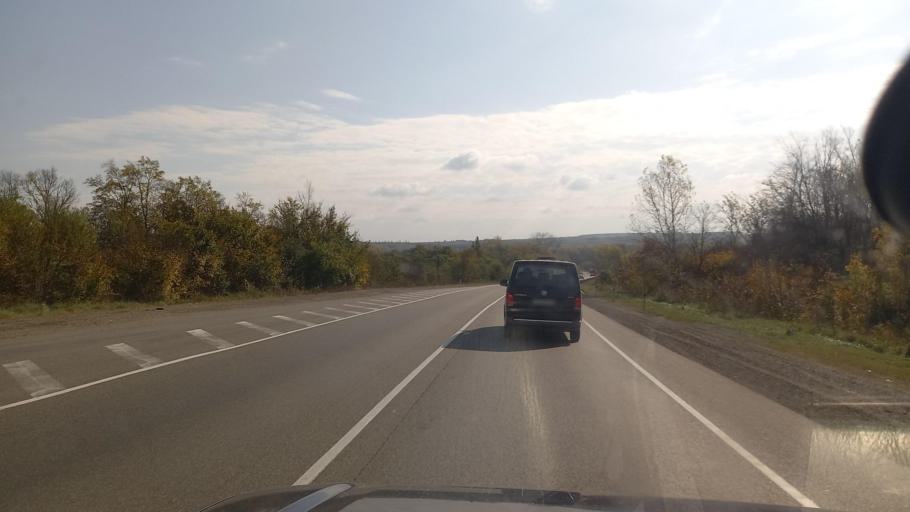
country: RU
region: Krasnodarskiy
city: Abinsk
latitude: 44.8474
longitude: 38.1478
